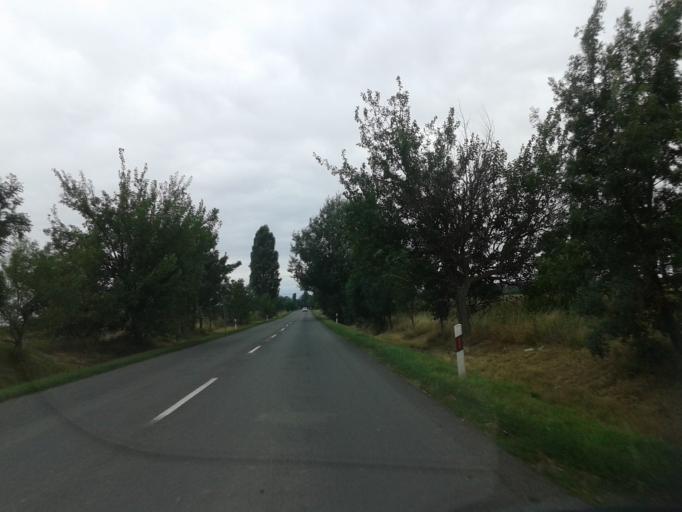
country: HU
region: Pest
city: Dunavarsany
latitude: 47.2483
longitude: 19.0231
